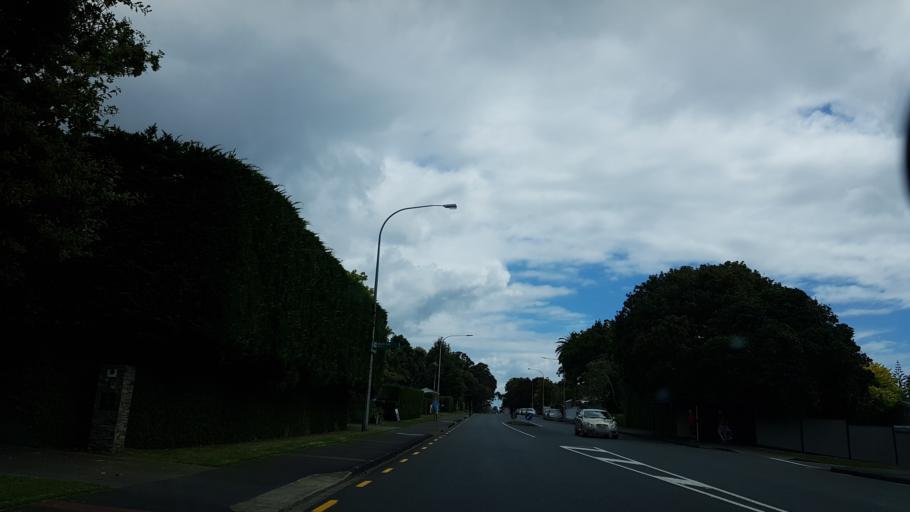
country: NZ
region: Auckland
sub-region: Auckland
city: North Shore
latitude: -36.7818
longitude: 174.7739
